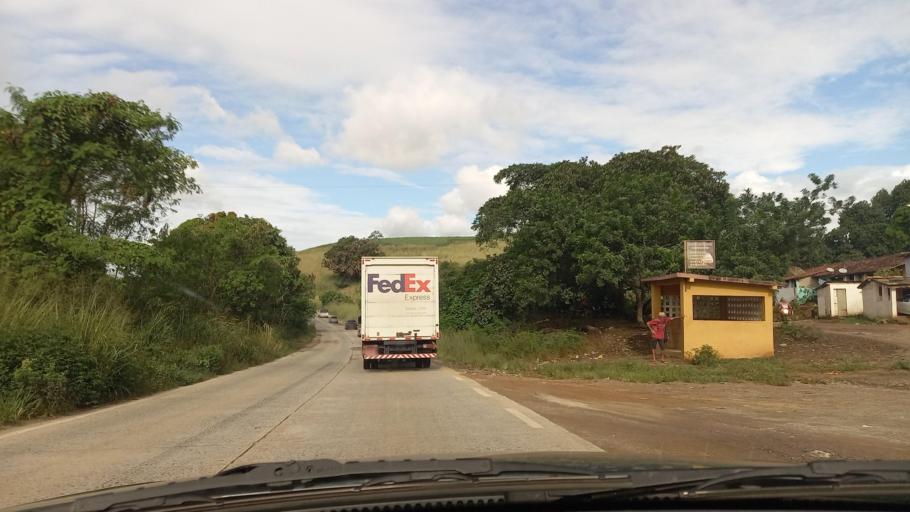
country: BR
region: Pernambuco
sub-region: Catende
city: Catende
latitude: -8.6949
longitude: -35.6969
